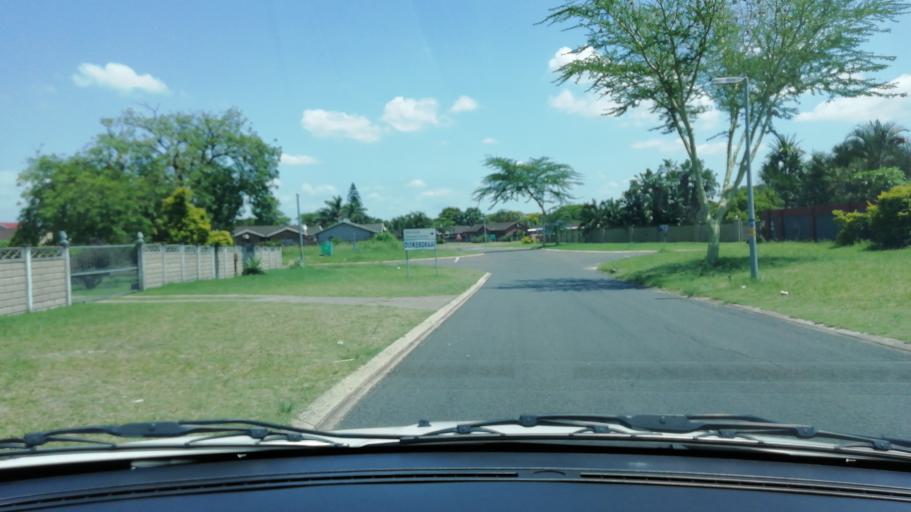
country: ZA
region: KwaZulu-Natal
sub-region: uThungulu District Municipality
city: Richards Bay
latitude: -28.7356
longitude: 32.0520
